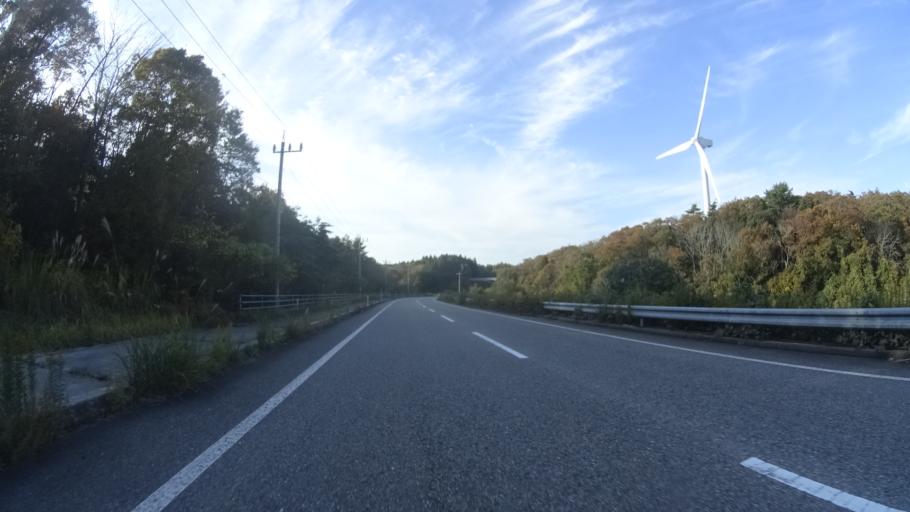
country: JP
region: Ishikawa
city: Hakui
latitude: 37.0737
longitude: 136.7324
